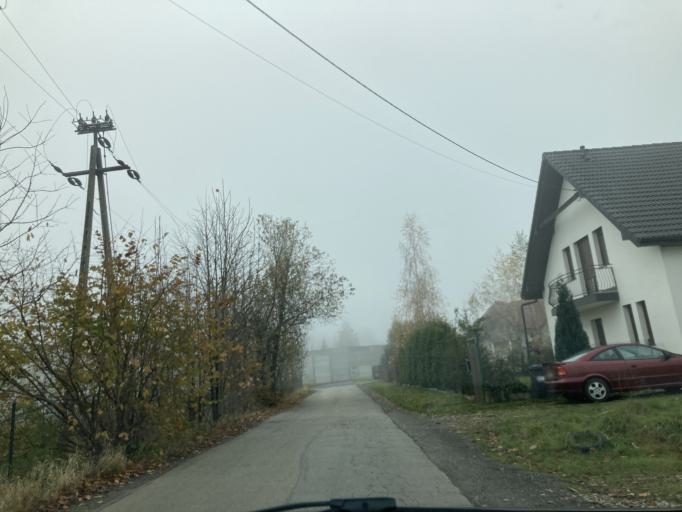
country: PL
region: Silesian Voivodeship
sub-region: Powiat bielski
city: Mazancowice
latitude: 49.8483
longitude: 19.0137
